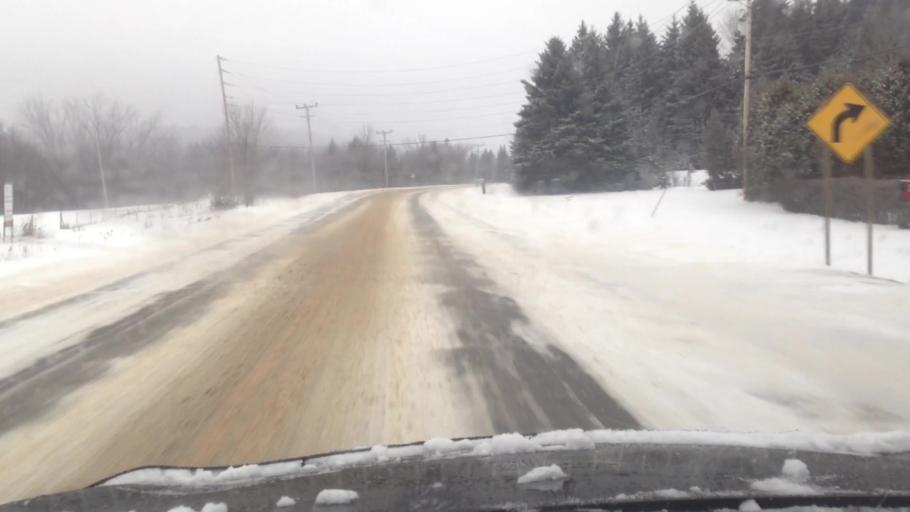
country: CA
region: Quebec
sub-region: Laurentides
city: Mont-Tremblant
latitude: 46.0935
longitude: -74.6074
